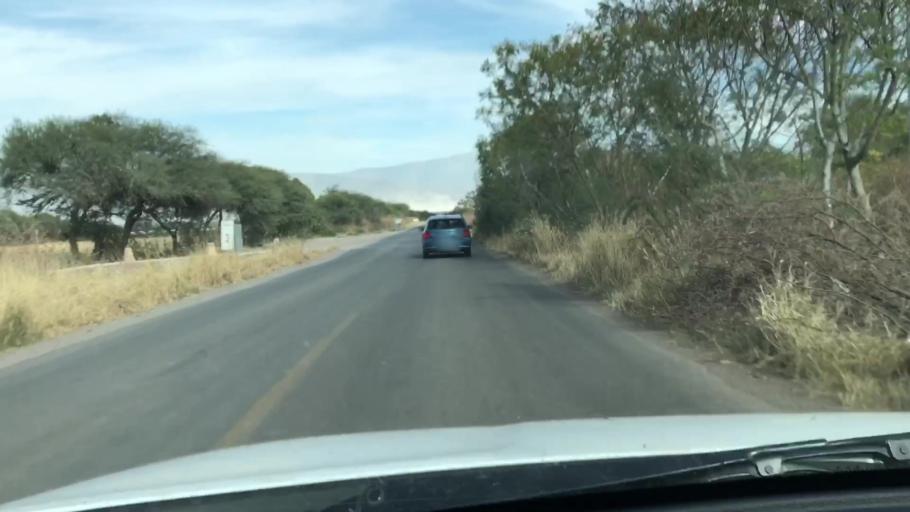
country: MX
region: Jalisco
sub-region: Zacoalco de Torres
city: Barranca de Otates (Barranca de Otatan)
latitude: 20.2777
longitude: -103.6267
